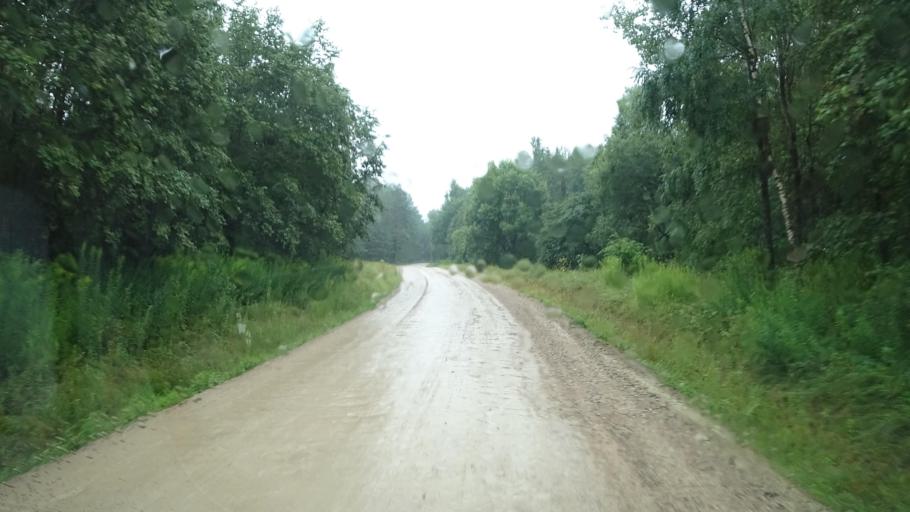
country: LV
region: Lecava
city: Iecava
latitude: 56.6616
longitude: 24.1701
